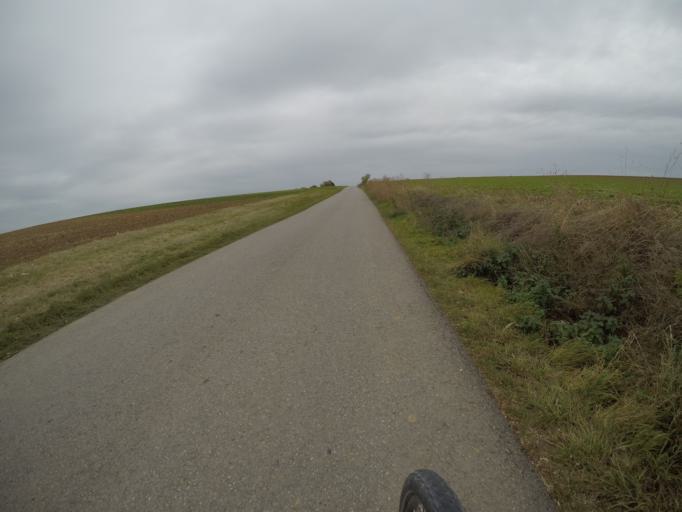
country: DE
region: Baden-Wuerttemberg
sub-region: Regierungsbezirk Stuttgart
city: Eberdingen
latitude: 48.8455
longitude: 8.9845
